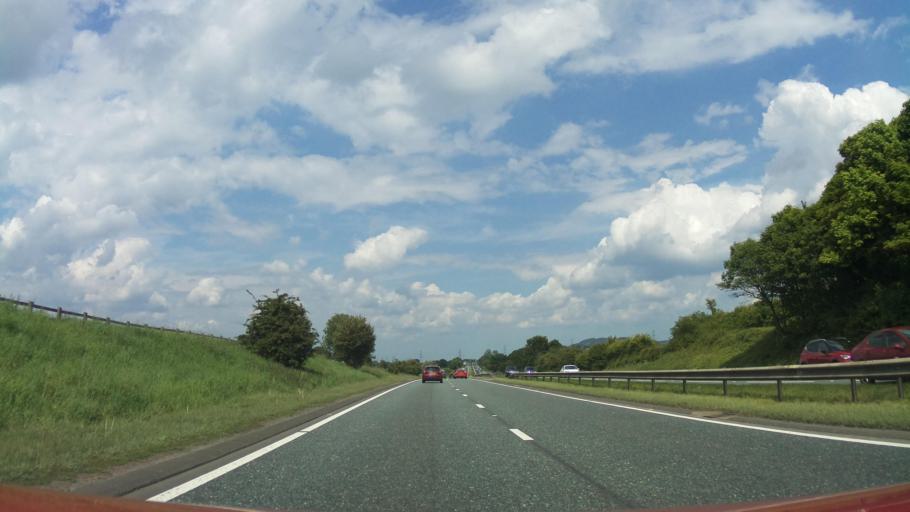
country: GB
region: England
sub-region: North Yorkshire
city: Thirsk
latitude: 54.3265
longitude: -1.3386
